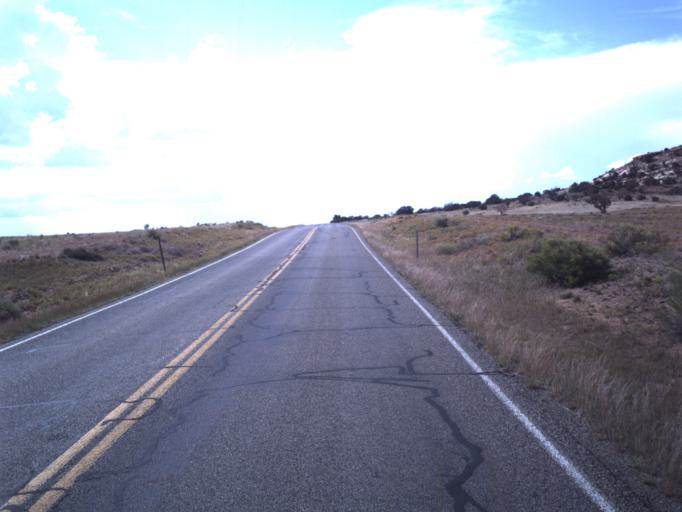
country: US
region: Utah
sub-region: Grand County
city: Moab
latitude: 38.5505
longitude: -109.7824
